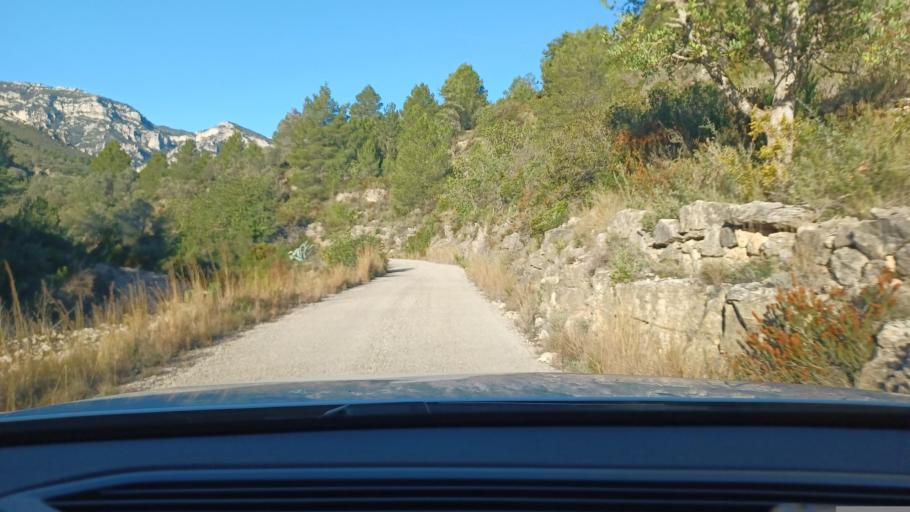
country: ES
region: Catalonia
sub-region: Provincia de Tarragona
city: Mas de Barberans
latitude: 40.7216
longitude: 0.3455
